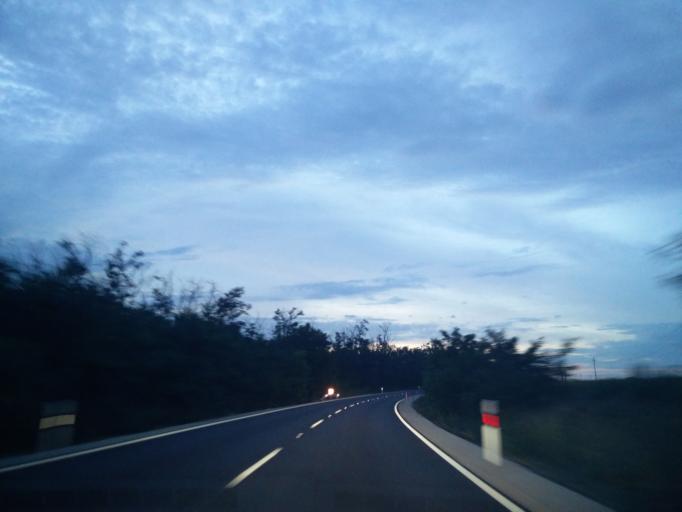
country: HU
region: Fejer
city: Lovasbereny
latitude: 47.2760
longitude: 18.5253
